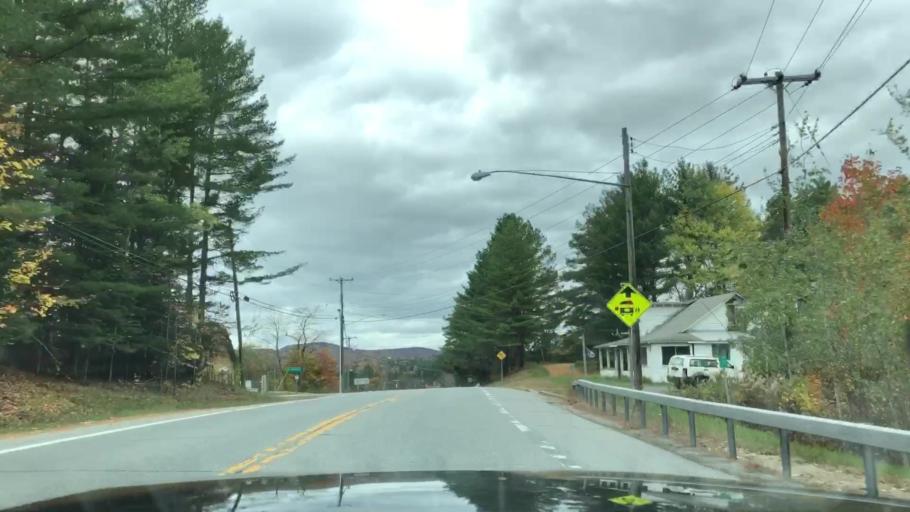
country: US
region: New York
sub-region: Franklin County
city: Tupper Lake
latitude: 43.9682
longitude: -74.4136
